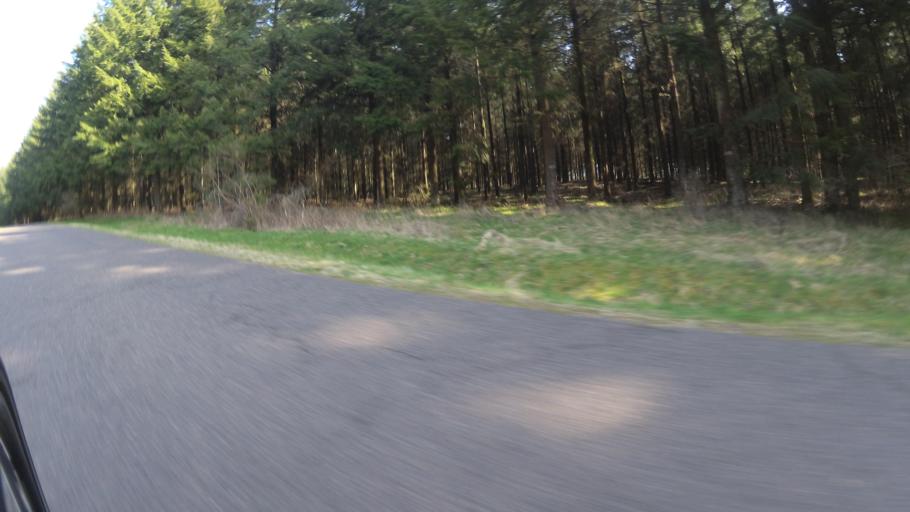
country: DE
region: Saarland
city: Freisen
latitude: 49.5608
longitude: 7.2567
